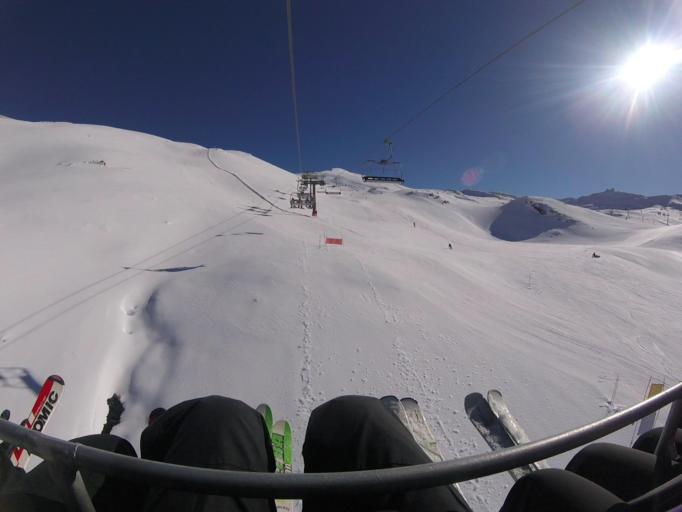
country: ES
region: Andalusia
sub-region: Provincia de Granada
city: Guejar-Sierra
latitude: 37.0726
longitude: -3.3838
